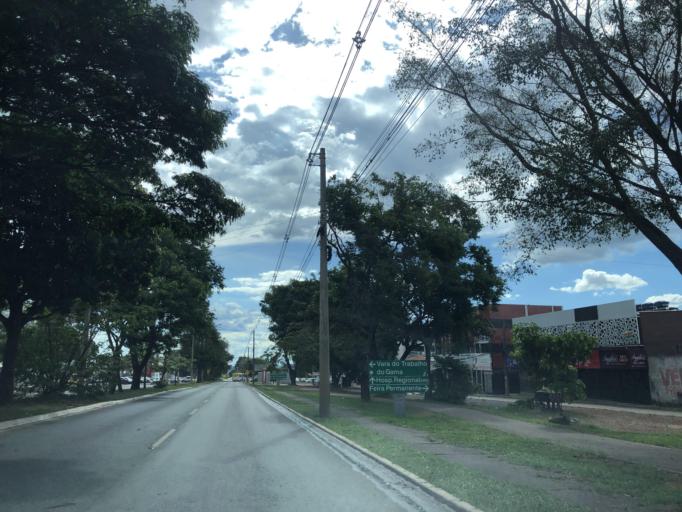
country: BR
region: Goias
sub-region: Luziania
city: Luziania
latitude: -16.0117
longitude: -48.0660
